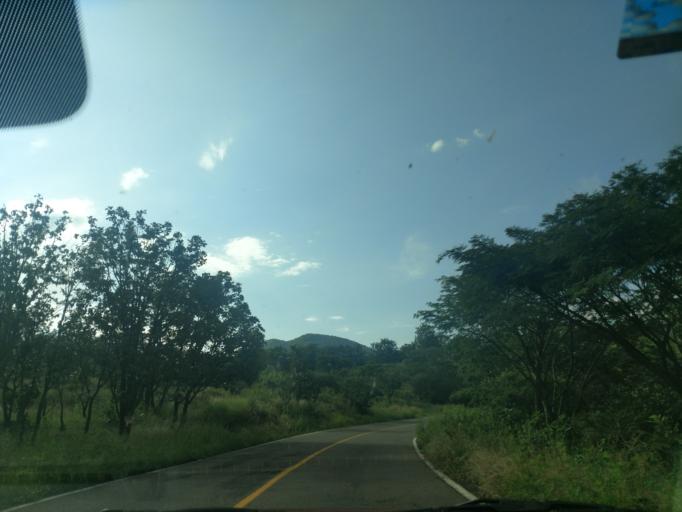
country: MX
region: Jalisco
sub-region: Atengo
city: Soyatlan del Oro
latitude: 20.5005
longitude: -104.3546
